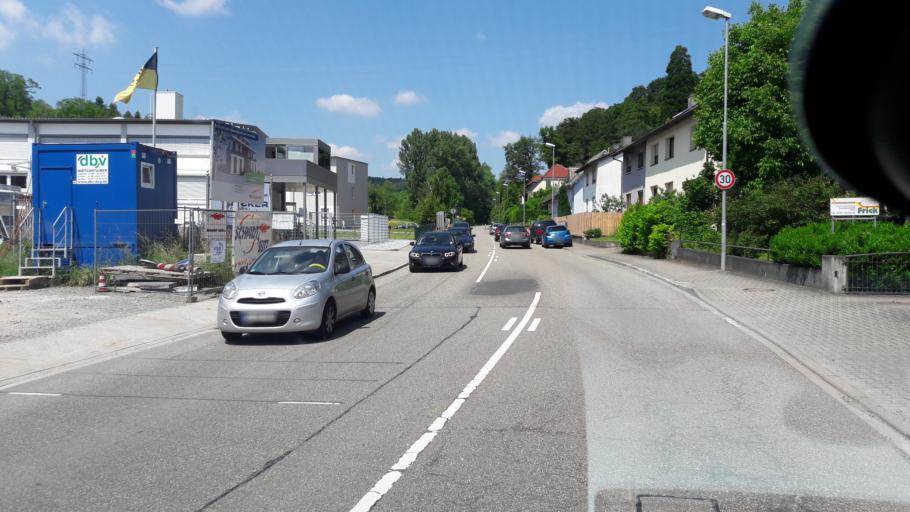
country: DE
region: Baden-Wuerttemberg
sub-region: Karlsruhe Region
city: Weingarten
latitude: 49.0095
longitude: 8.5324
